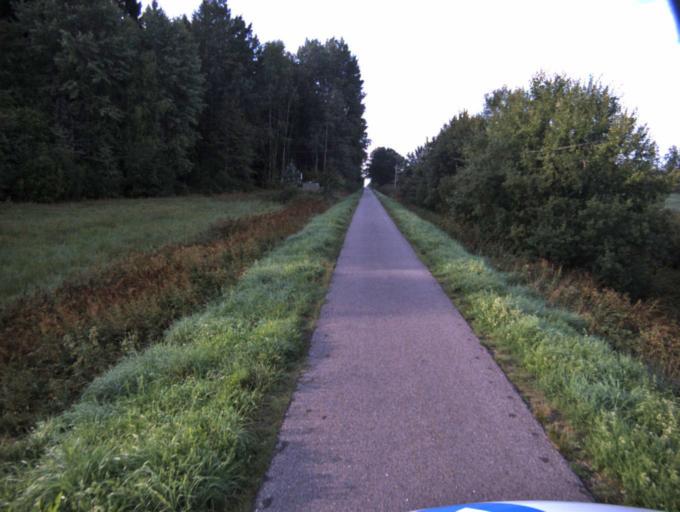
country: SE
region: Vaestra Goetaland
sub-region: Ulricehamns Kommun
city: Ulricehamn
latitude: 57.7689
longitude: 13.4017
